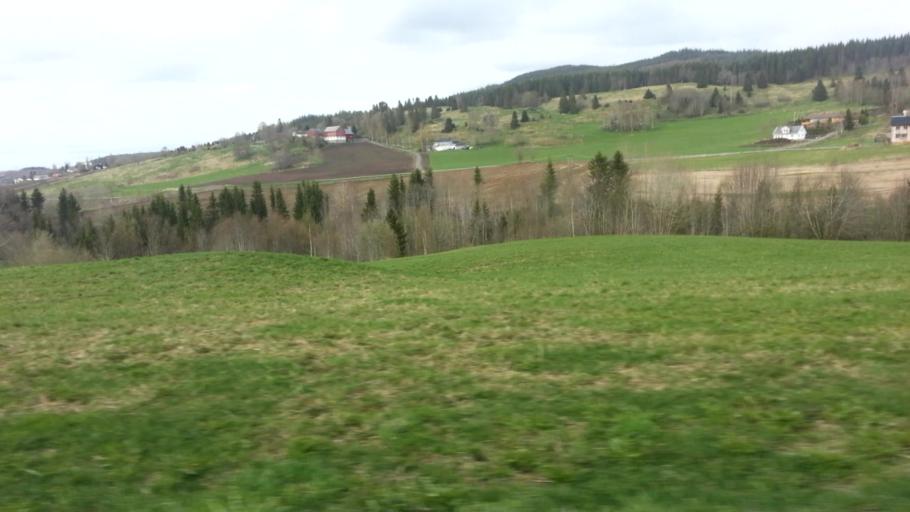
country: NO
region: Nord-Trondelag
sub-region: Levanger
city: Skogn
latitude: 63.6586
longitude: 11.2349
